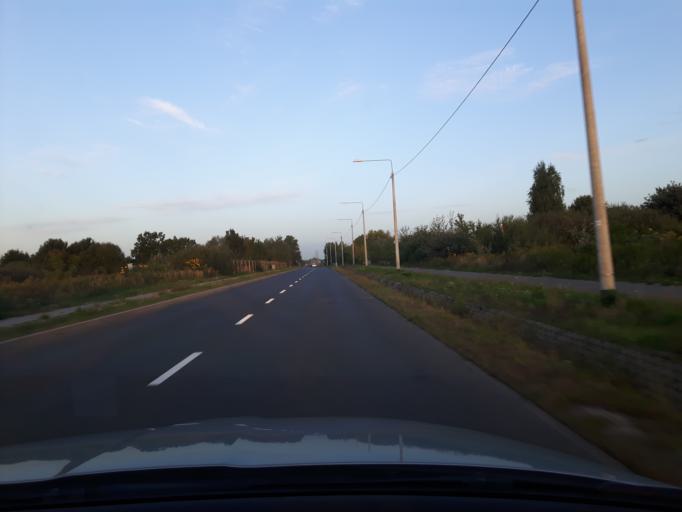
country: PL
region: Masovian Voivodeship
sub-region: Warszawa
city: Wawer
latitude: 52.1849
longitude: 21.1647
